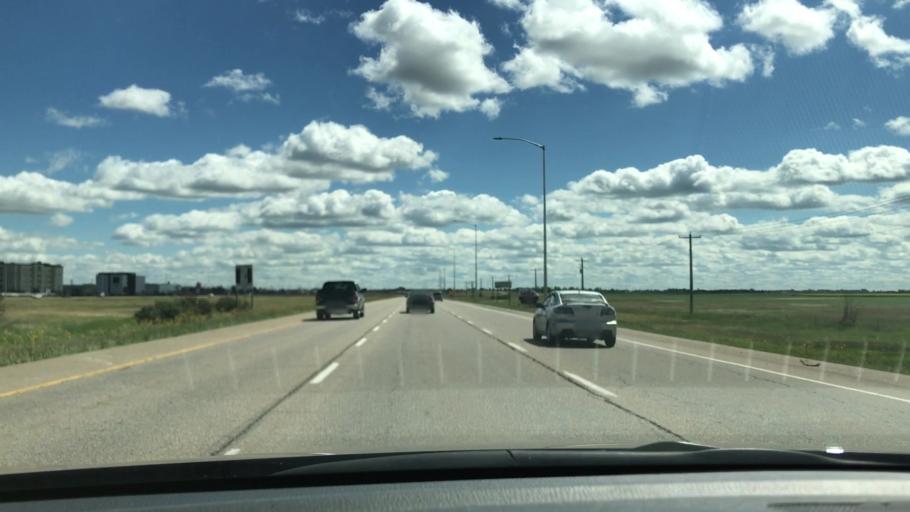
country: CA
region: Alberta
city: Leduc
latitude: 53.2976
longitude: -113.5499
